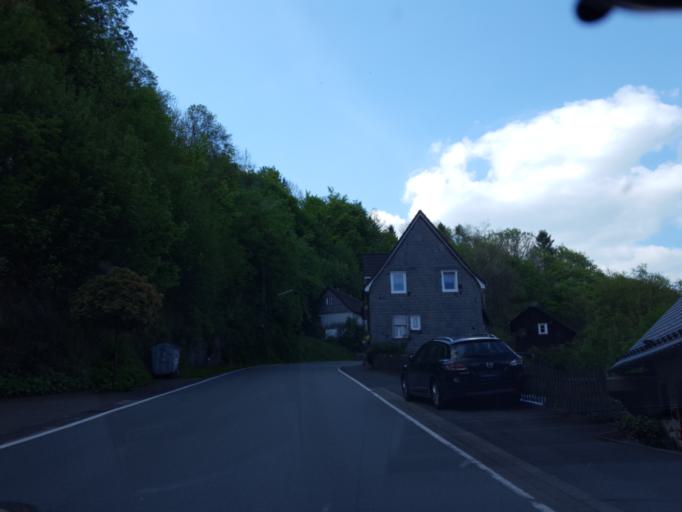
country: DE
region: North Rhine-Westphalia
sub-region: Regierungsbezirk Arnsberg
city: Winterberg
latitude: 51.2533
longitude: 8.4673
